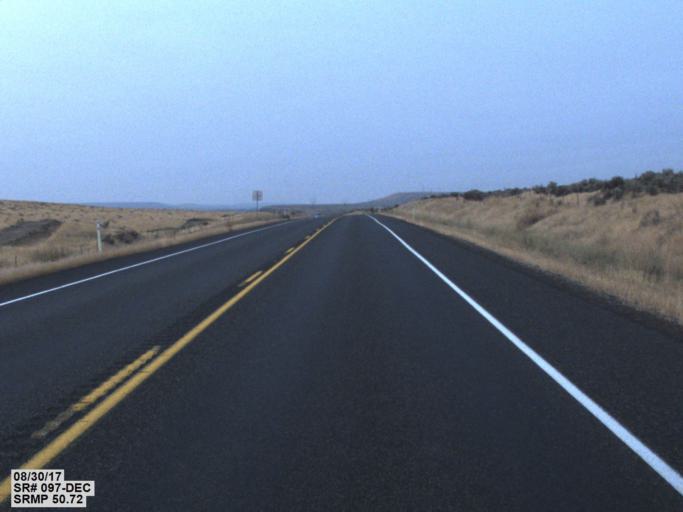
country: US
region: Washington
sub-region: Yakima County
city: Toppenish
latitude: 46.2512
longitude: -120.4145
